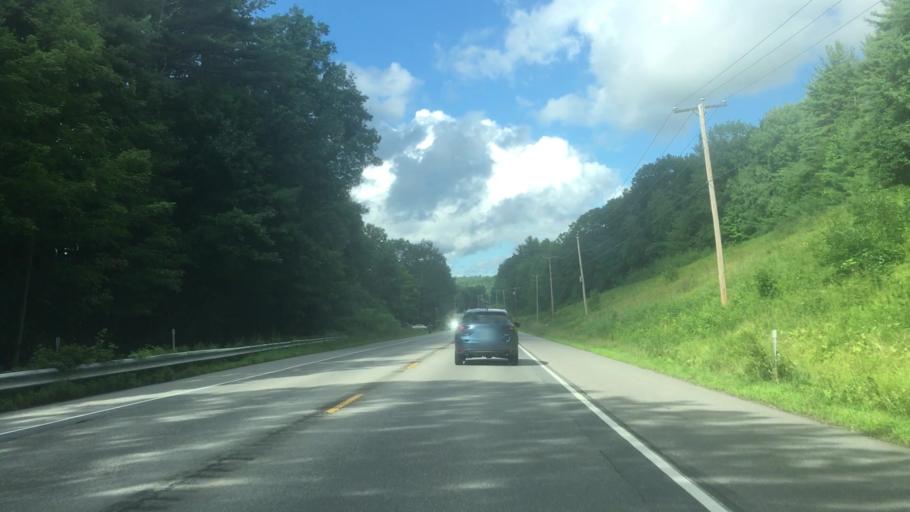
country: US
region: New Hampshire
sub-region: Cheshire County
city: Chesterfield
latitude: 42.9045
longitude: -72.4186
